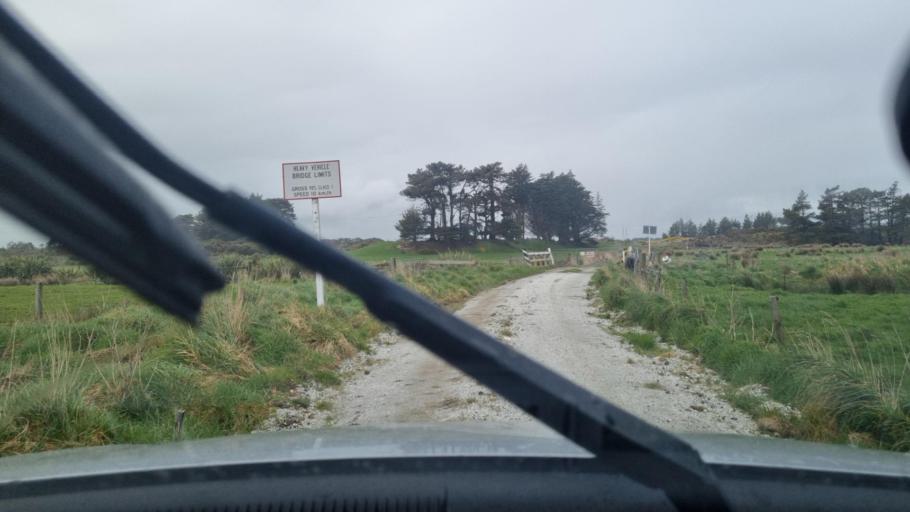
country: NZ
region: Southland
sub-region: Invercargill City
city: Bluff
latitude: -46.5118
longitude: 168.4115
